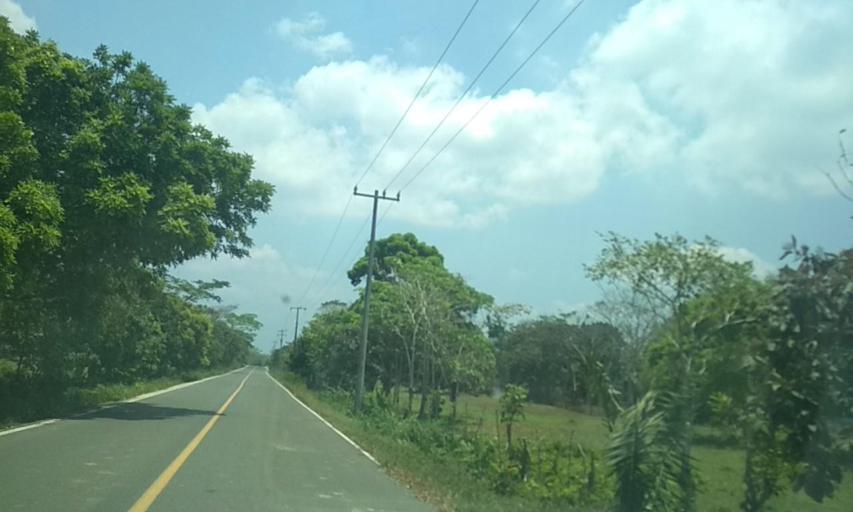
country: MX
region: Tabasco
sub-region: Huimanguillo
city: Francisco Rueda
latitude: 17.7491
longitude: -94.0385
